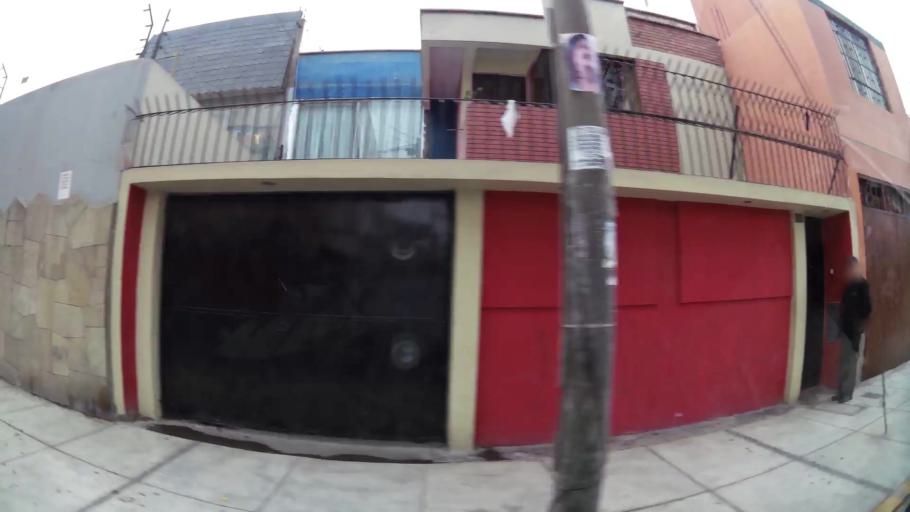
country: PE
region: Lima
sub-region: Lima
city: Surco
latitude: -12.1427
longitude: -77.0184
